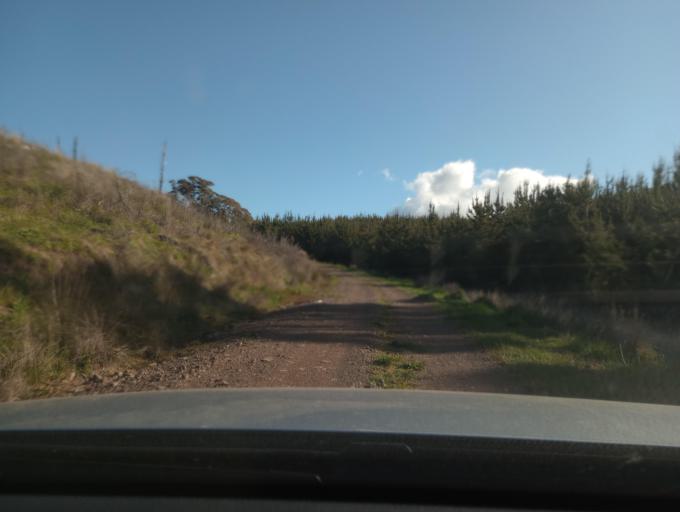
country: AU
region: New South Wales
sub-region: Blayney
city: Blayney
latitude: -33.4139
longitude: 149.3151
